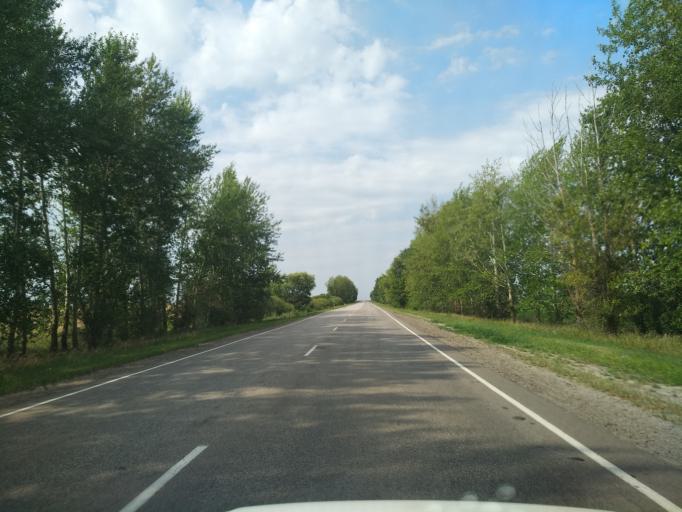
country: RU
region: Voronezj
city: Verkhnyaya Khava
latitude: 51.6974
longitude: 39.9584
